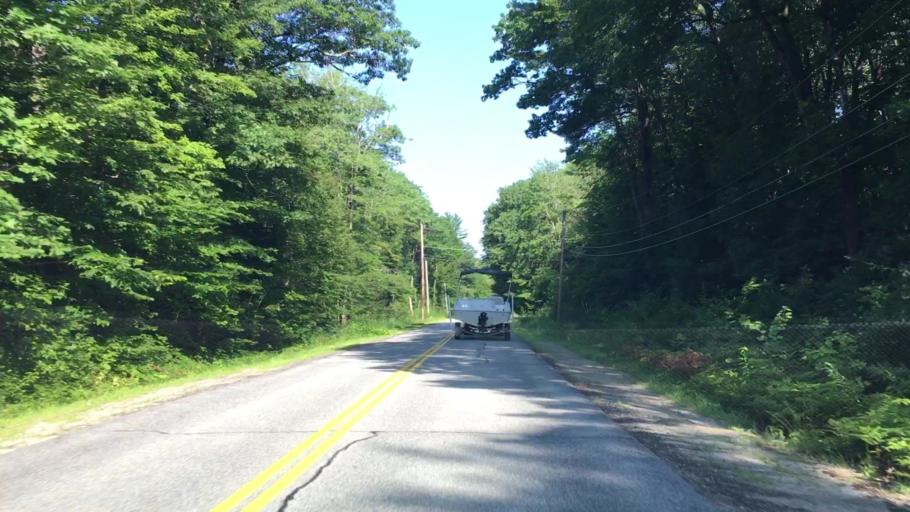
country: US
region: Maine
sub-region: Androscoggin County
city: Poland
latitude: 44.0526
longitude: -70.3737
